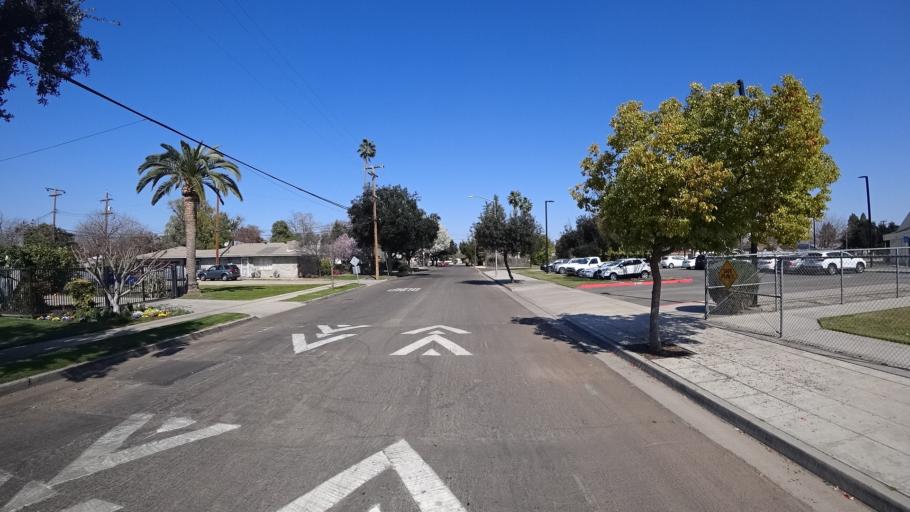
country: US
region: California
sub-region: Fresno County
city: Fresno
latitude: 36.7560
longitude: -119.7928
